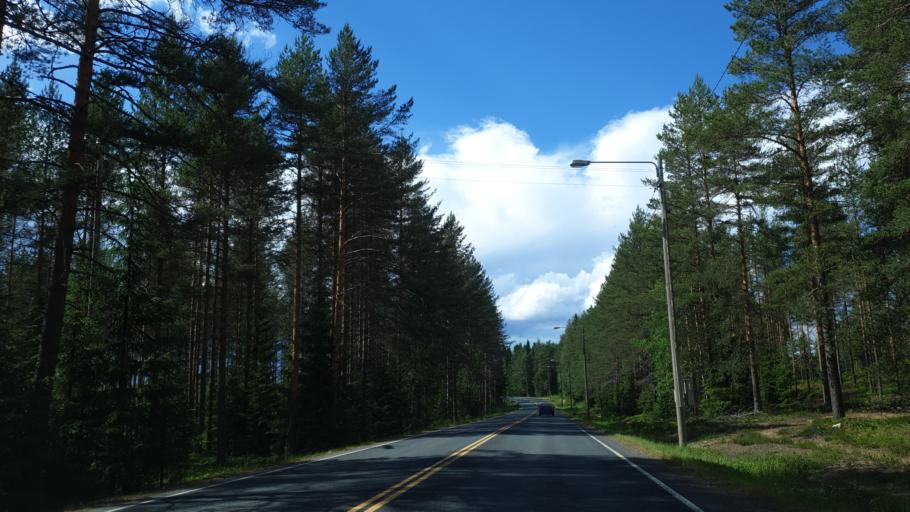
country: FI
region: Northern Savo
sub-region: Kuopio
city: Vehmersalmi
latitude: 62.9154
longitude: 28.1431
